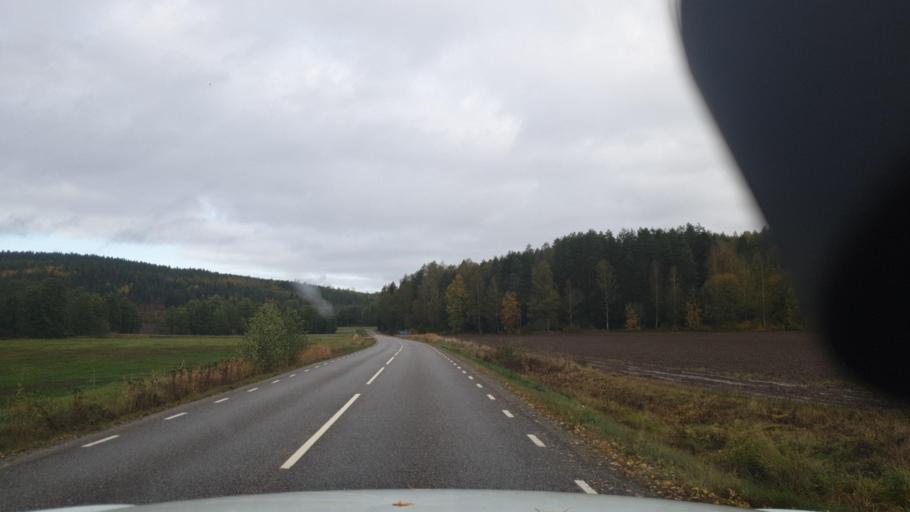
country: SE
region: Vaermland
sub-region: Grums Kommun
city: Grums
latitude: 59.3980
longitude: 13.0704
